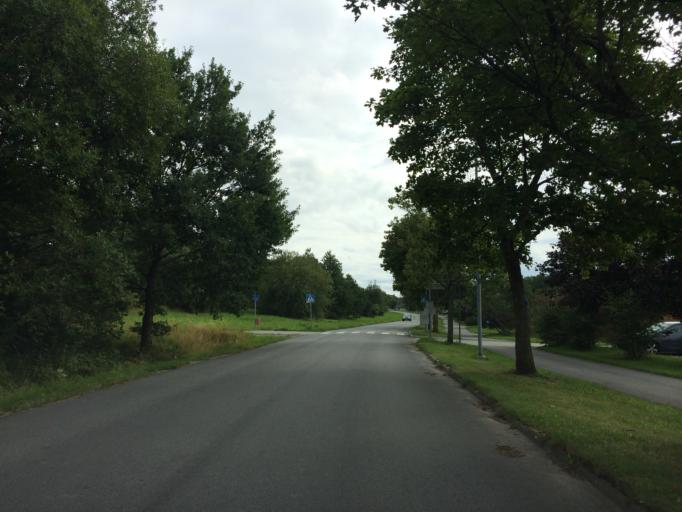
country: SE
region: Stockholm
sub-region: Upplands Vasby Kommun
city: Upplands Vaesby
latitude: 59.4646
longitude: 17.9095
